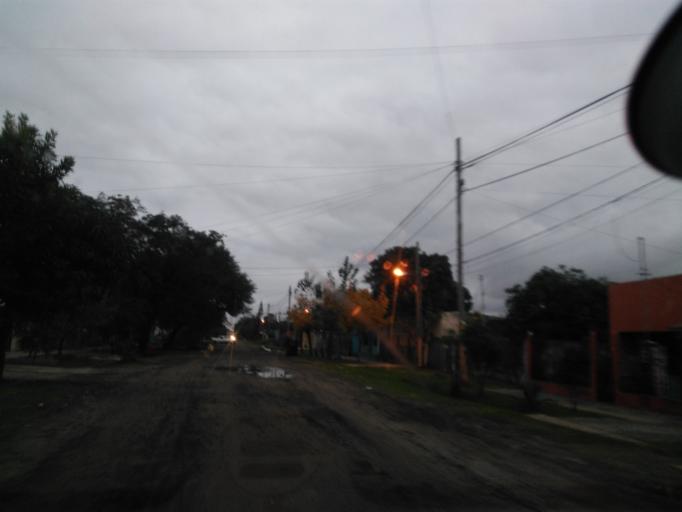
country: AR
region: Chaco
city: Resistencia
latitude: -27.4767
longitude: -58.9903
